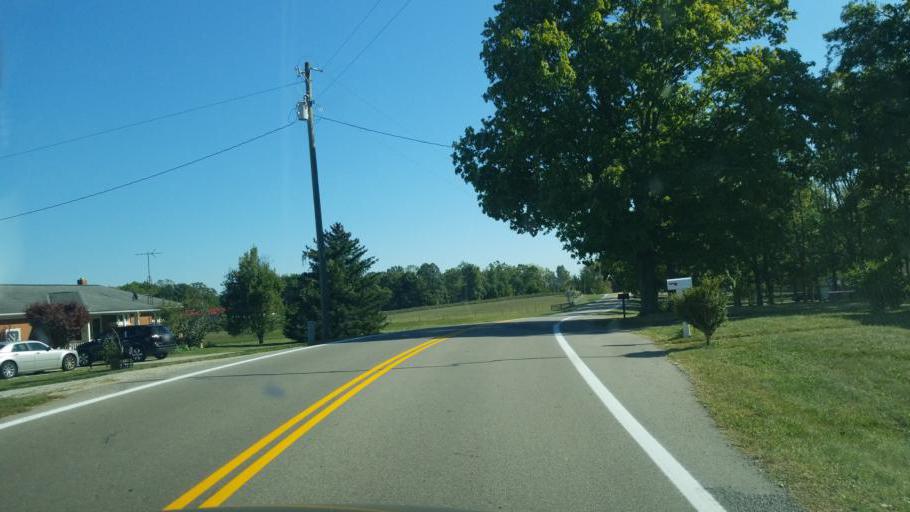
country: US
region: Ohio
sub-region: Champaign County
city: Mechanicsburg
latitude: 40.1094
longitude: -83.5811
